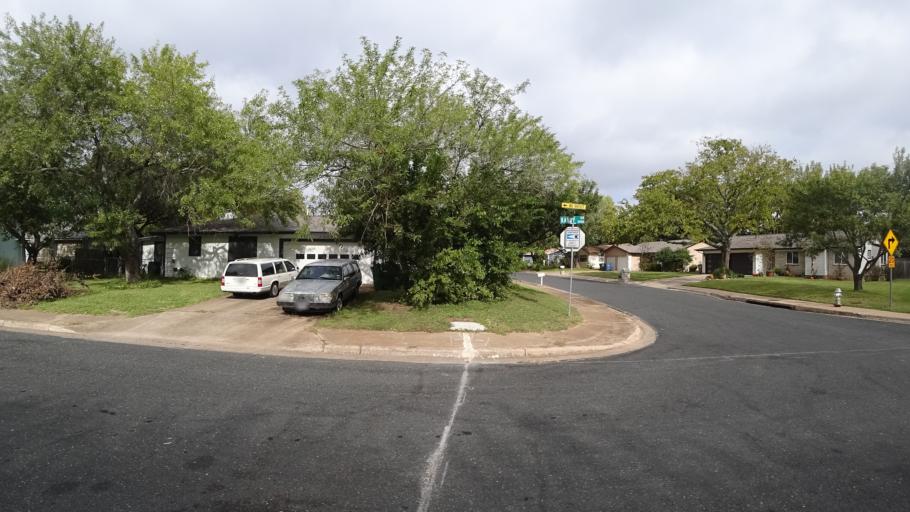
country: US
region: Texas
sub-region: Travis County
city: Shady Hollow
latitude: 30.2115
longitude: -97.8386
